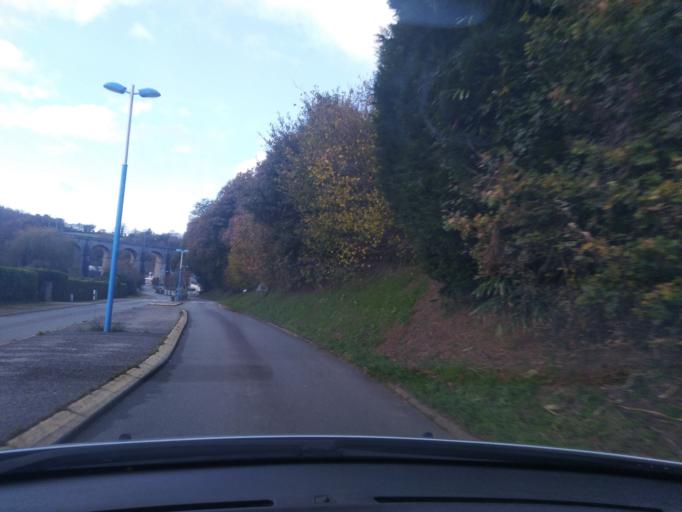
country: FR
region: Brittany
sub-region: Departement du Finistere
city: Plouigneau
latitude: 48.5633
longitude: -3.6343
